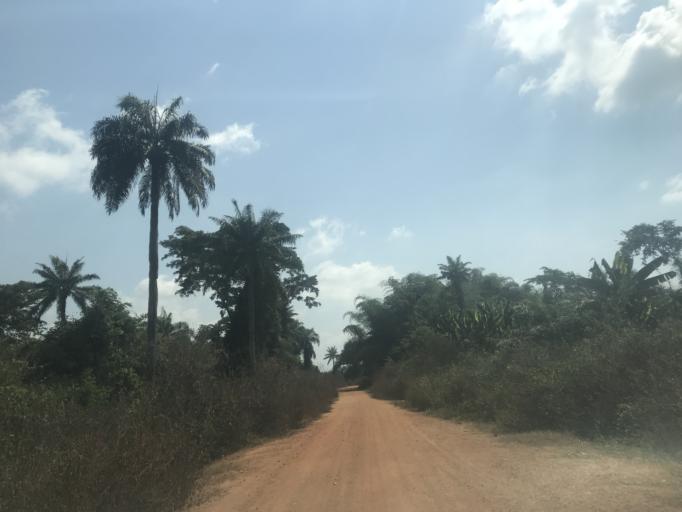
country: NG
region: Osun
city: Oke Mesi
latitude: 7.8925
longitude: 4.8785
